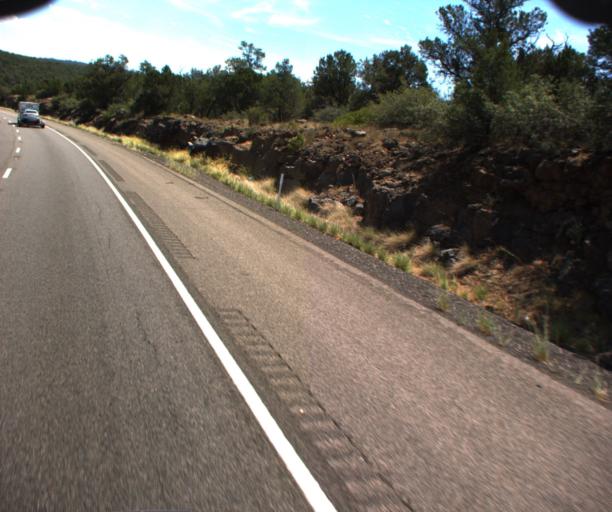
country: US
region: Arizona
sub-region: Yavapai County
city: Village of Oak Creek (Big Park)
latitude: 34.7684
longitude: -111.6427
